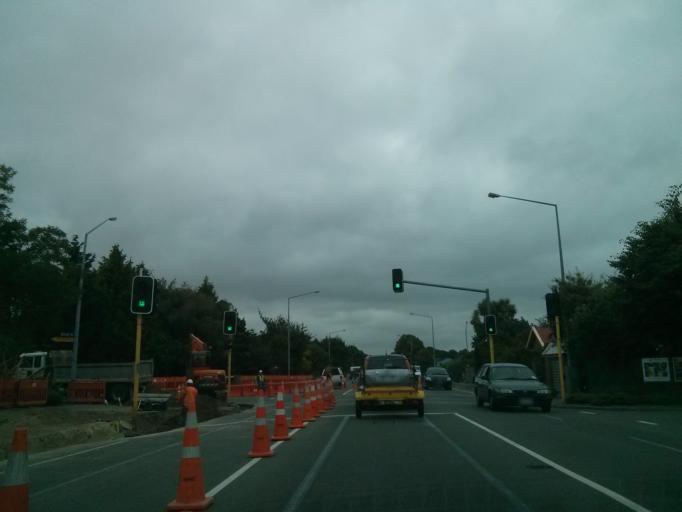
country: NZ
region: Canterbury
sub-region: Christchurch City
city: Christchurch
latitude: -43.5360
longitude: 172.5679
